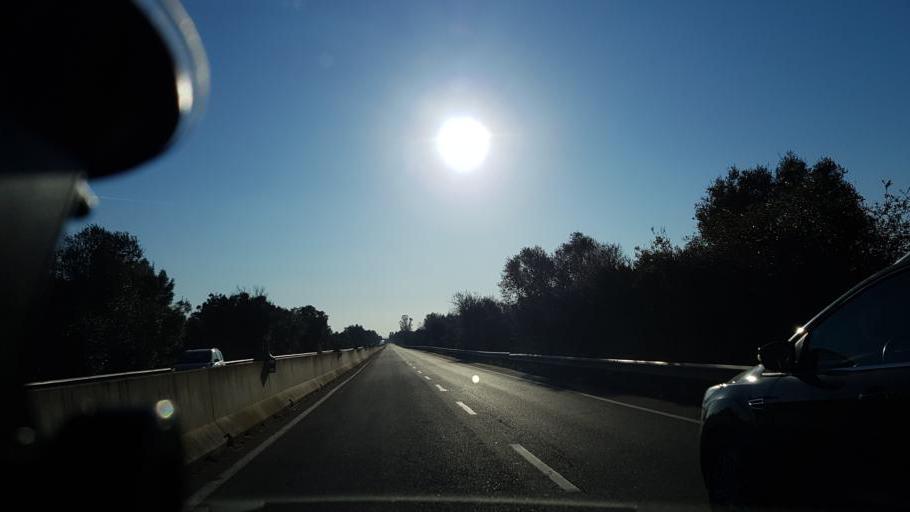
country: IT
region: Apulia
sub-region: Provincia di Lecce
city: Merine
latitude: 40.3768
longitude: 18.2562
